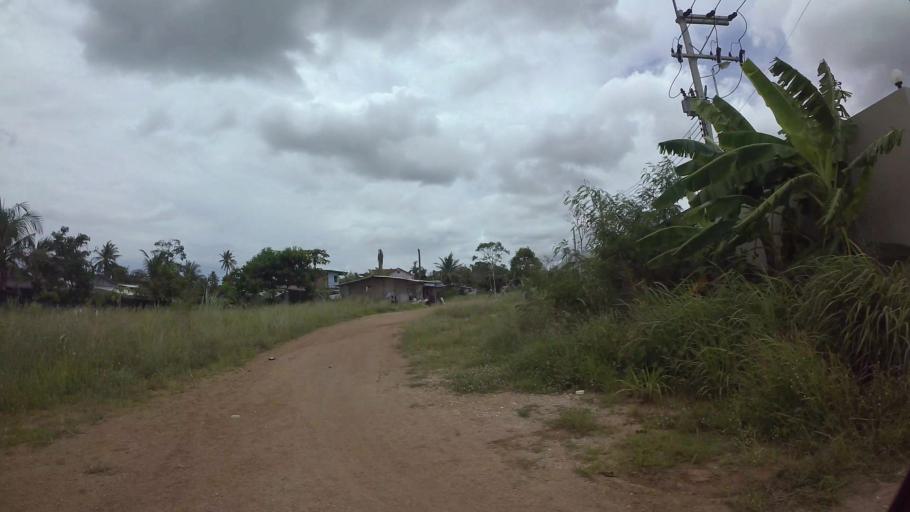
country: TH
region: Chon Buri
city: Si Racha
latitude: 13.1721
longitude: 100.9718
